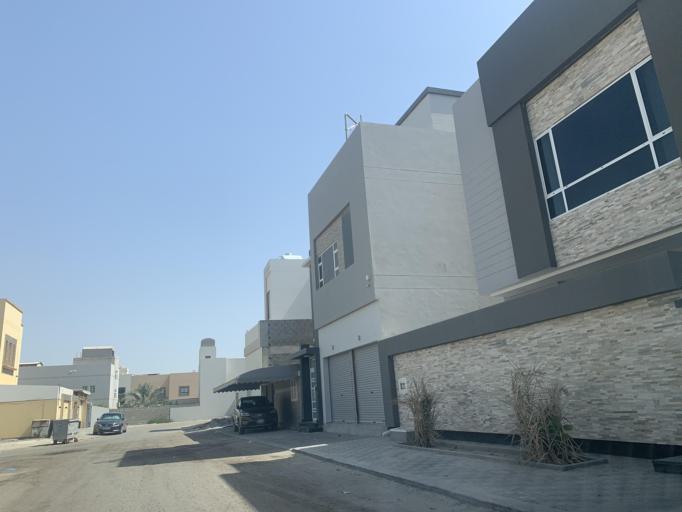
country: BH
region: Manama
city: Jidd Hafs
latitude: 26.2334
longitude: 50.5072
